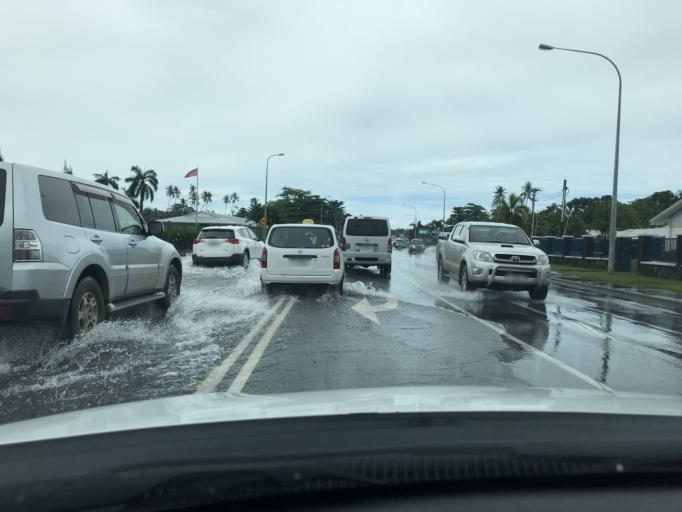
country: WS
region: Tuamasaga
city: Vaiusu
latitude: -13.8377
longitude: -171.7824
